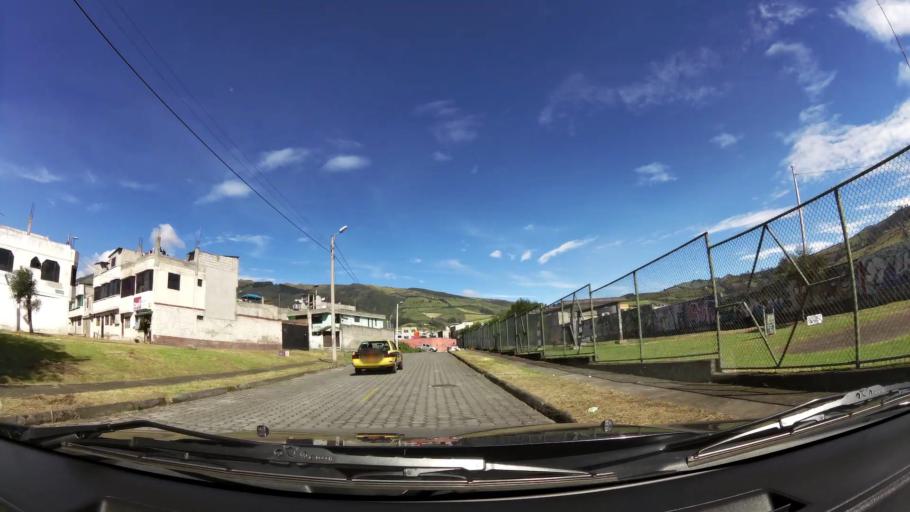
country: EC
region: Pichincha
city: Quito
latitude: -0.2896
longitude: -78.5628
